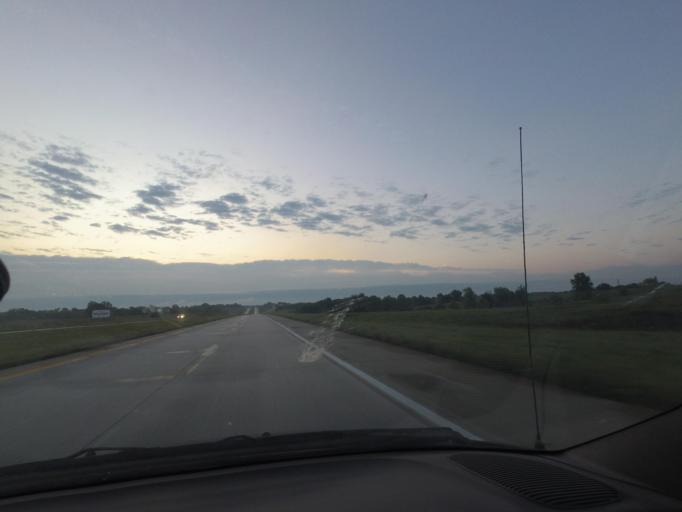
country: US
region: Missouri
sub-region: Macon County
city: Macon
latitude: 39.7577
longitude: -92.6395
